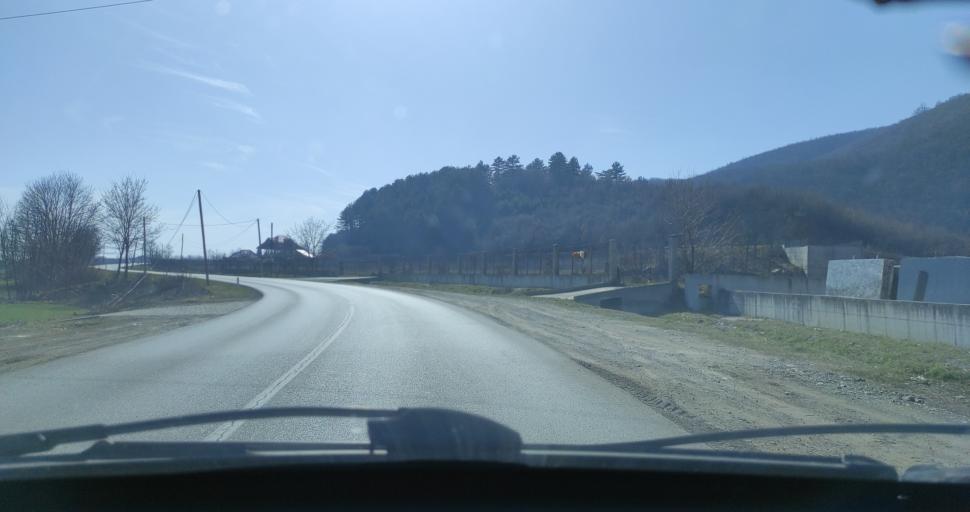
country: XK
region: Gjakova
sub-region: Komuna e Decanit
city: Strellc i Eperm
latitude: 42.5916
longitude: 20.2945
